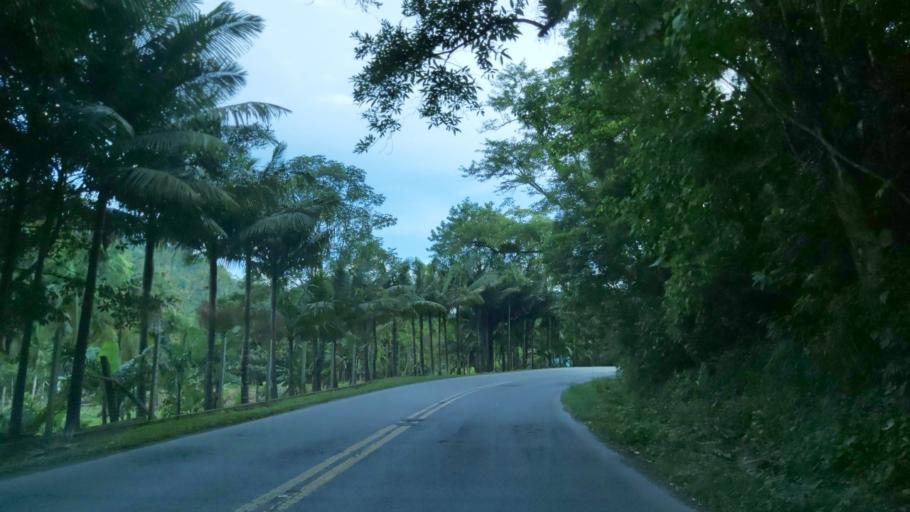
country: BR
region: Sao Paulo
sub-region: Miracatu
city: Miracatu
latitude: -24.0654
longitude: -47.5944
